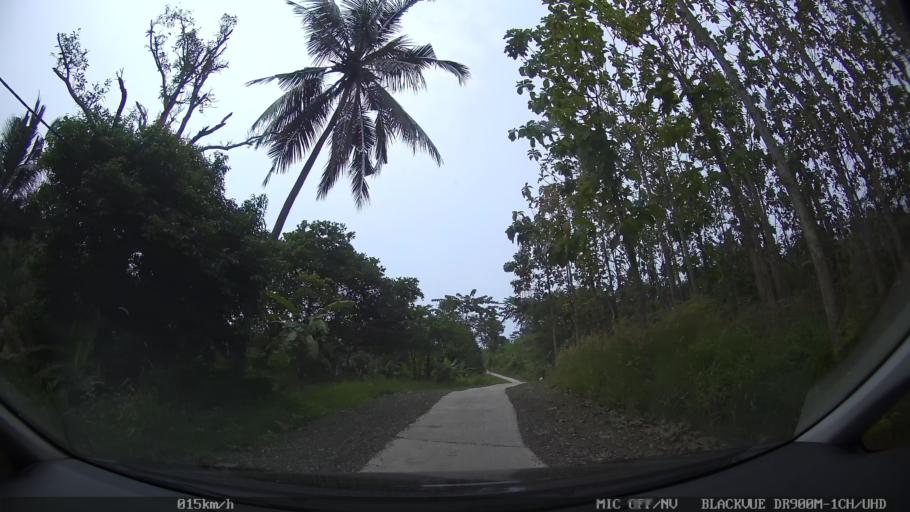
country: ID
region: Lampung
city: Panjang
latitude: -5.4279
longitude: 105.3095
